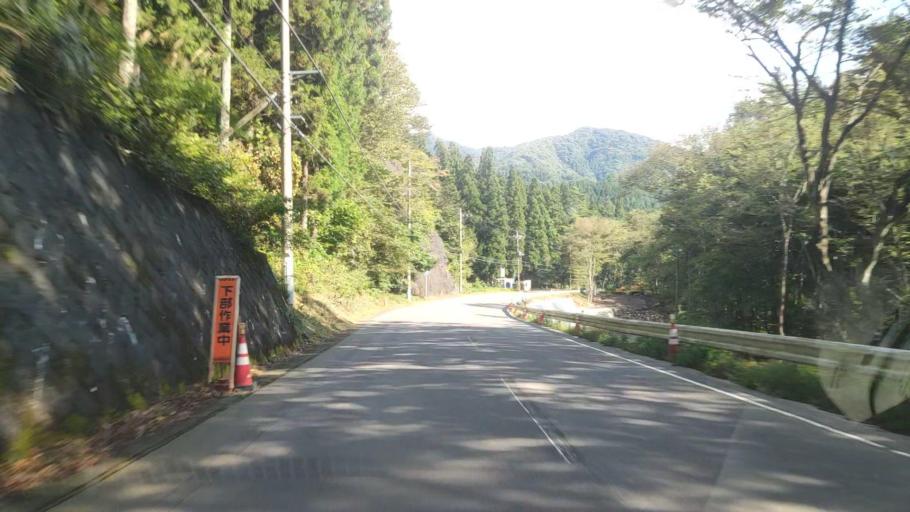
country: JP
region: Gunma
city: Nakanojomachi
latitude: 36.6144
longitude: 138.7408
